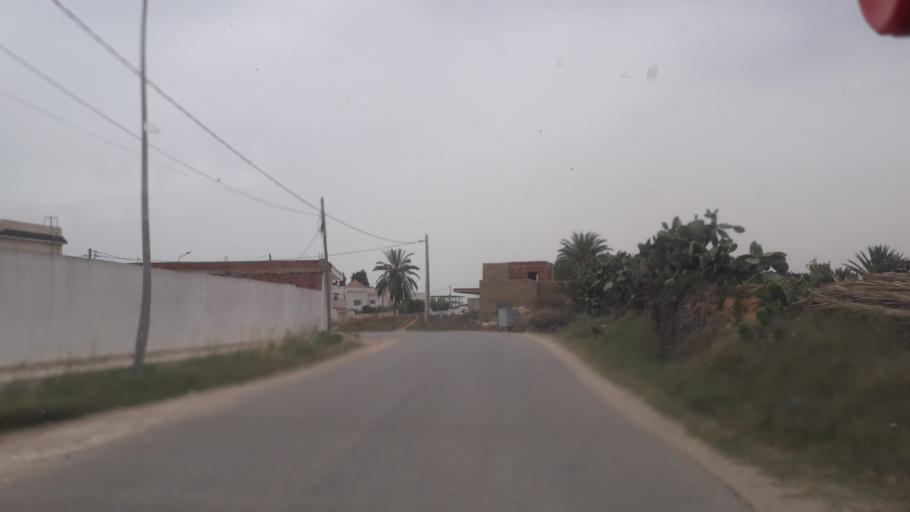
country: TN
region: Safaqis
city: Al Qarmadah
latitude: 34.7930
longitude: 10.7640
